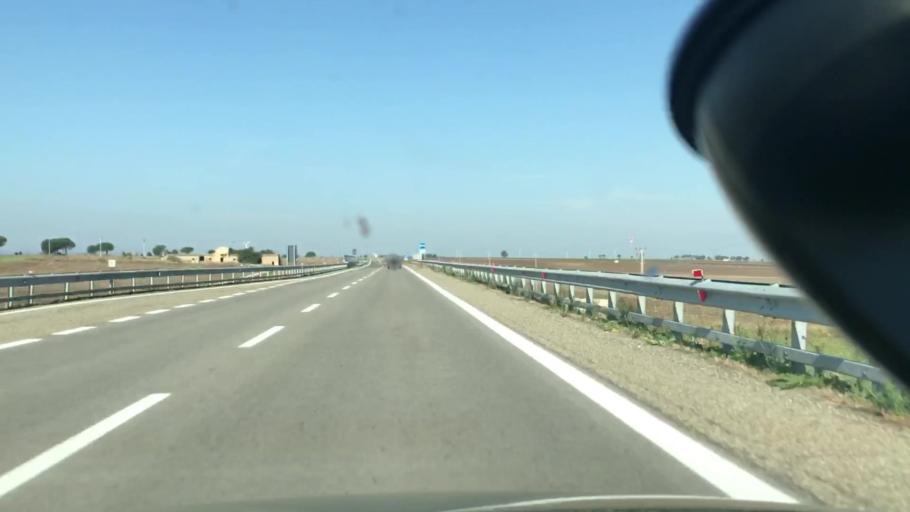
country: IT
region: Basilicate
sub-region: Provincia di Potenza
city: Montemilone
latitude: 40.9868
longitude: 15.9120
